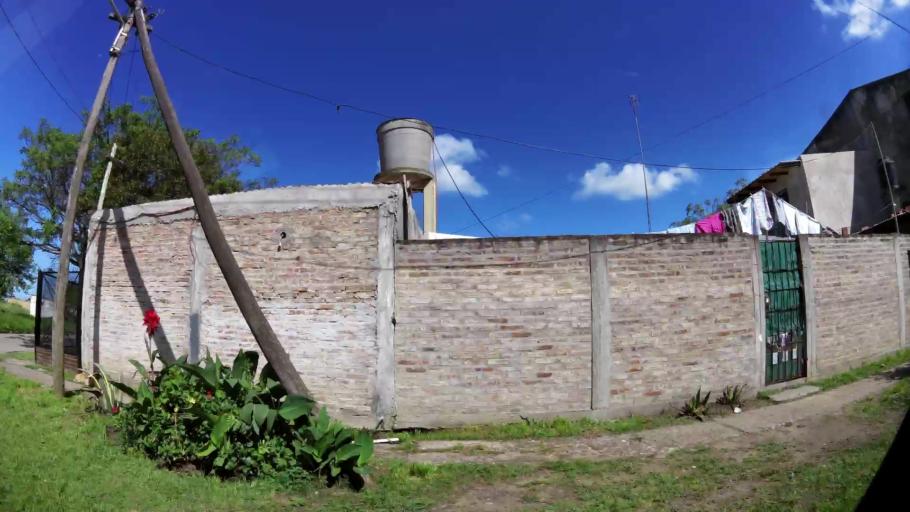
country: AR
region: Buenos Aires
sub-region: Partido de Quilmes
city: Quilmes
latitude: -34.8010
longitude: -58.2646
